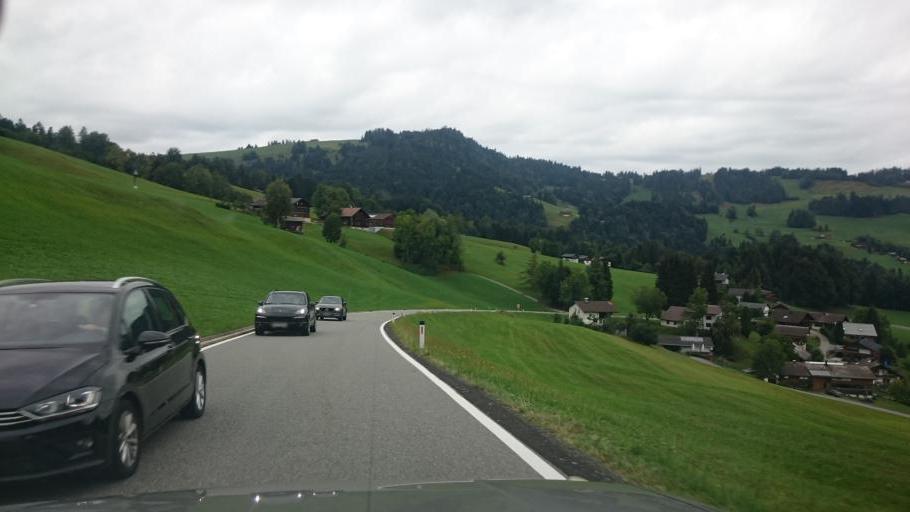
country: AT
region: Vorarlberg
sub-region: Politischer Bezirk Bregenz
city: Andelsbuch
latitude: 47.4133
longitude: 9.8395
